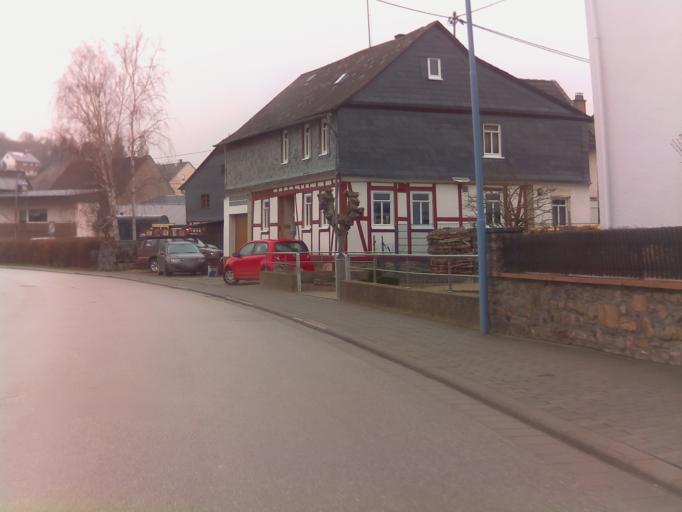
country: DE
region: Rheinland-Pfalz
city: Mengerschied
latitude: 49.9108
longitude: 7.5051
